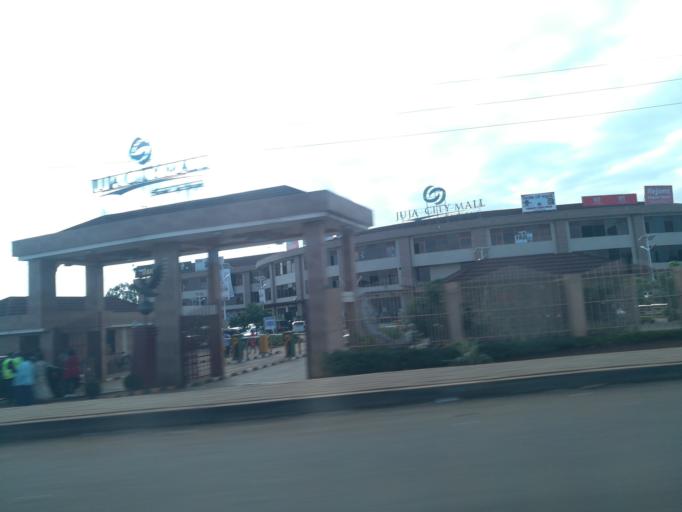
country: KE
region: Nairobi Area
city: Thika
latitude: -1.1186
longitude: 37.0096
